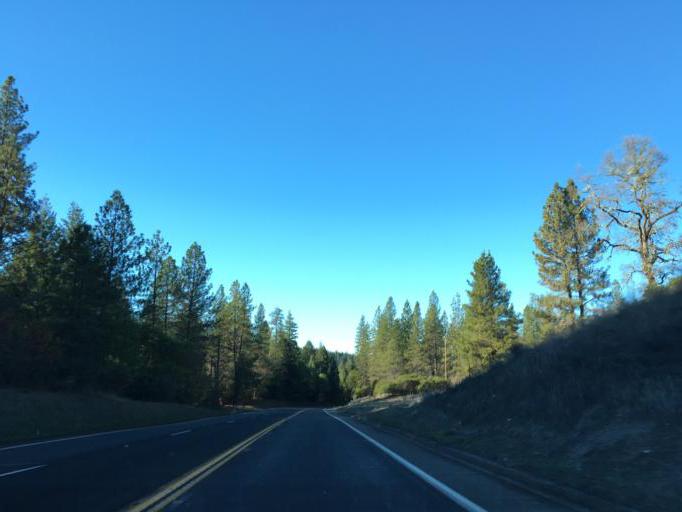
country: US
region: California
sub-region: Mendocino County
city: Laytonville
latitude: 39.7134
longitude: -123.4959
